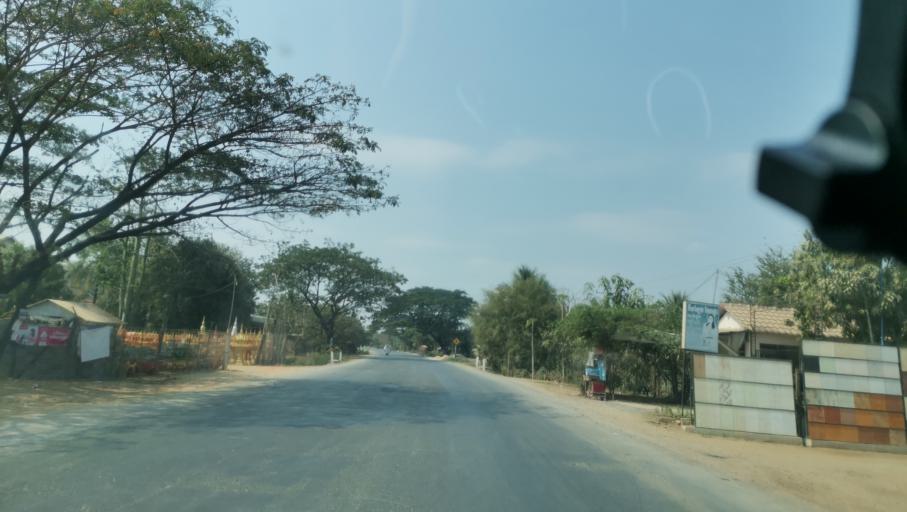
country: KH
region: Battambang
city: Battambang
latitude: 13.0693
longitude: 103.1637
